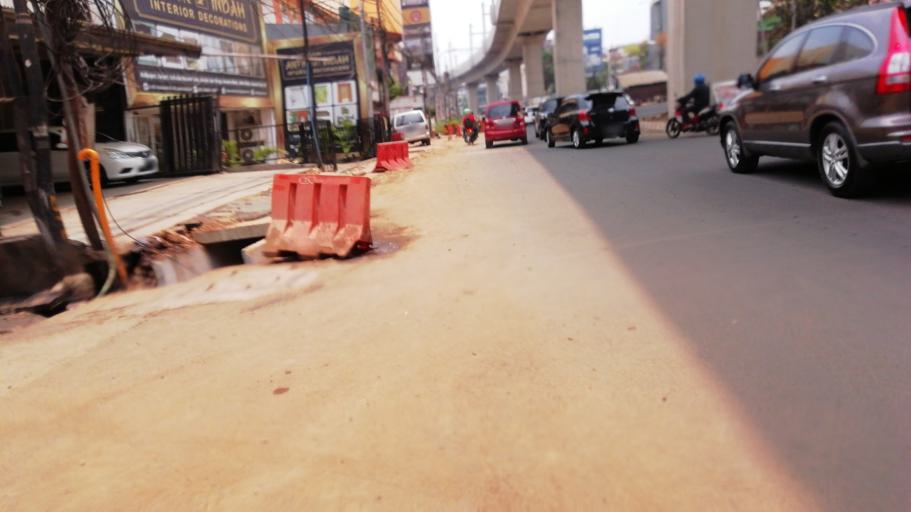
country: ID
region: Jakarta Raya
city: Jakarta
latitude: -6.2660
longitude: 106.7973
